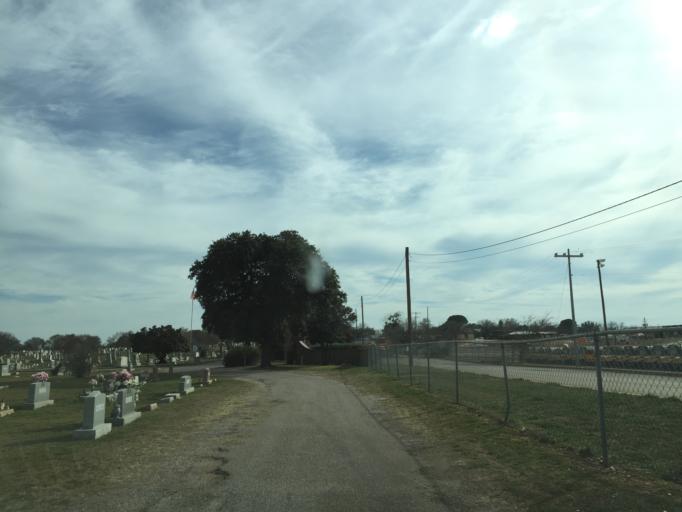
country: US
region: Texas
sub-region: Llano County
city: Llano
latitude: 30.7435
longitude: -98.6721
